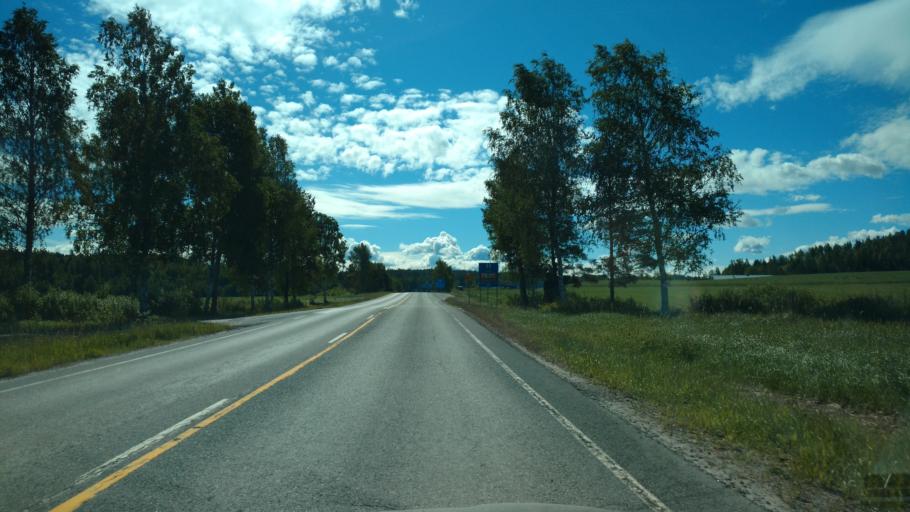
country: FI
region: Varsinais-Suomi
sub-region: Salo
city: Muurla
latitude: 60.3768
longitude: 23.3062
